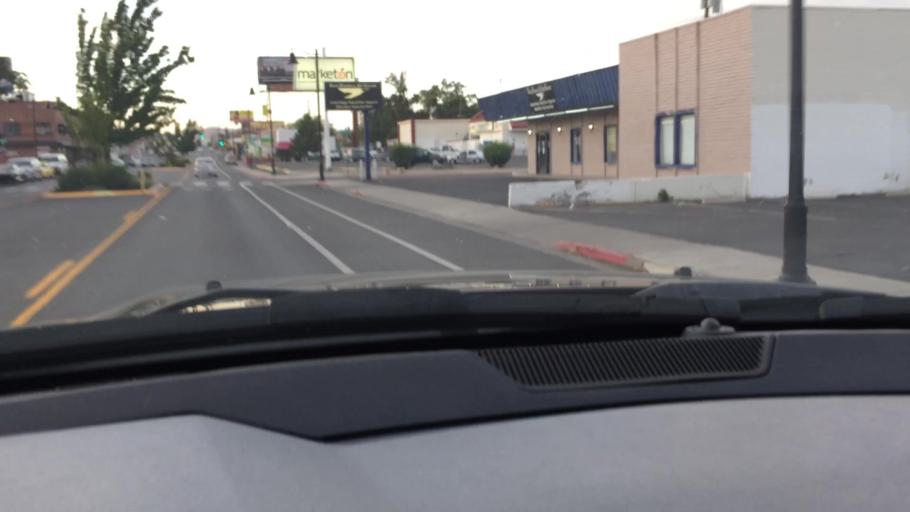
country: US
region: Nevada
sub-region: Washoe County
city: Reno
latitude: 39.5101
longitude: -119.8031
